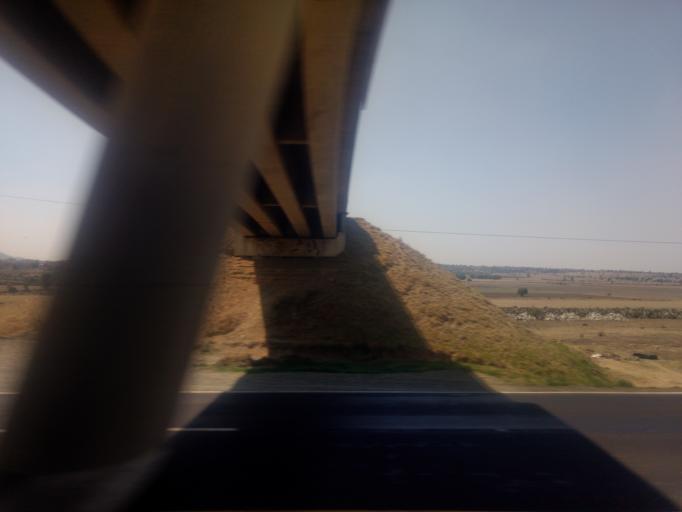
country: MX
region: Morelos
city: Nopaltepec
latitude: 19.7992
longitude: -98.7260
